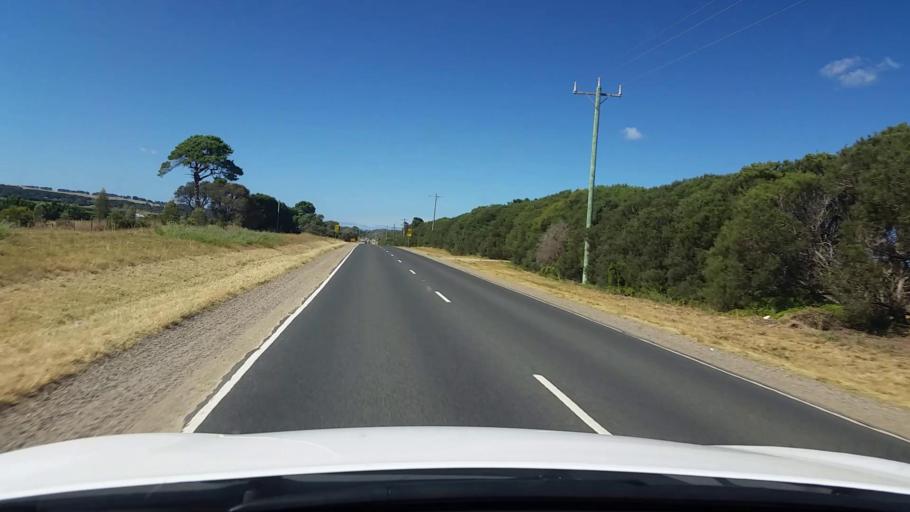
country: AU
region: Victoria
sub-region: Mornington Peninsula
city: Rosebud West
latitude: -38.4060
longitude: 144.8877
